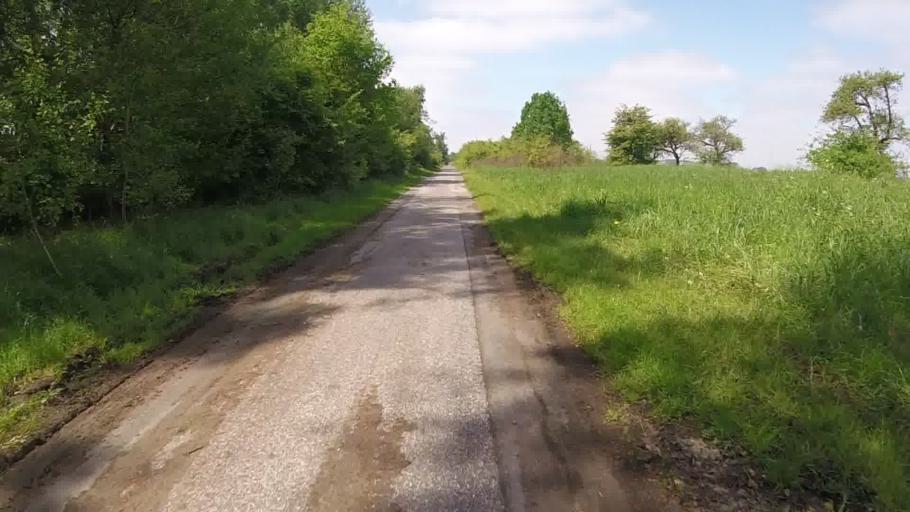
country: DE
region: Schleswig-Holstein
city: Oststeinbek
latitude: 53.4900
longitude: 10.1657
